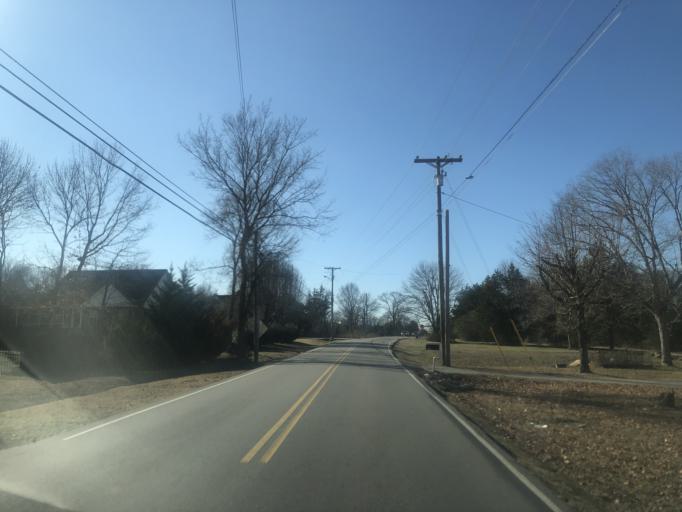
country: US
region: Tennessee
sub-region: Rutherford County
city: Smyrna
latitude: 35.9624
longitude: -86.5355
